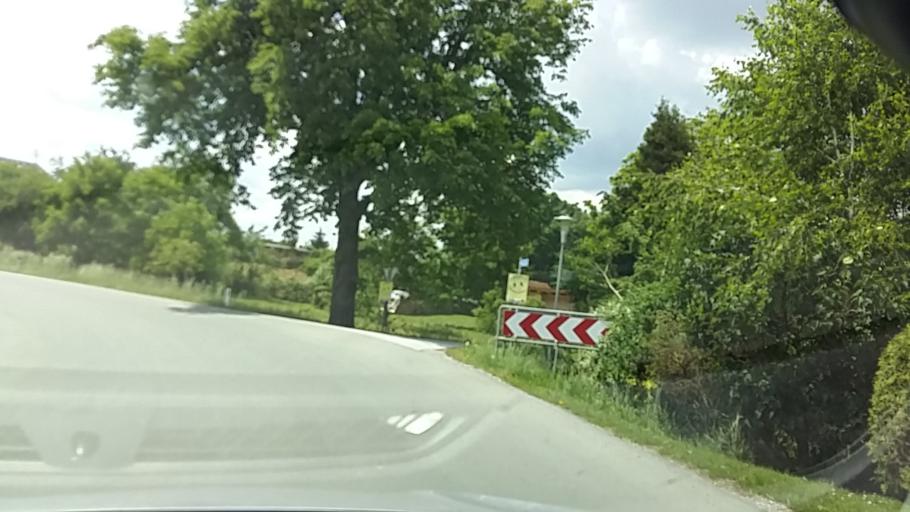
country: AT
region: Styria
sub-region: Politischer Bezirk Hartberg-Fuerstenfeld
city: Bad Blumau
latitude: 47.1171
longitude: 15.9999
